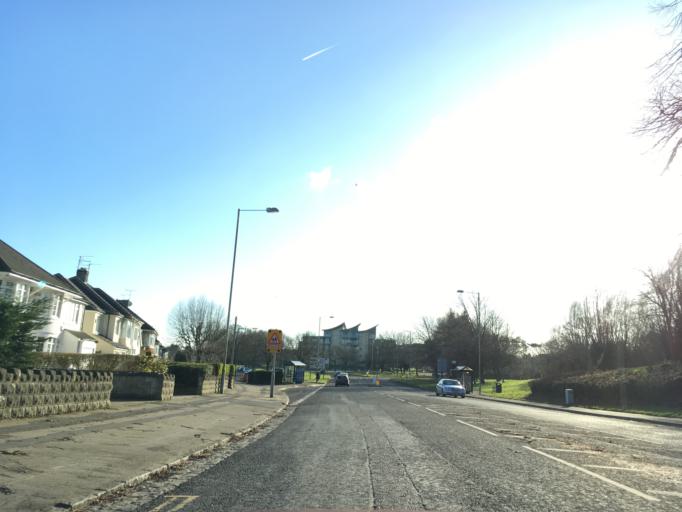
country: GB
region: England
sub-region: Borough of Swindon
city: Swindon
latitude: 51.5476
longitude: -1.7715
